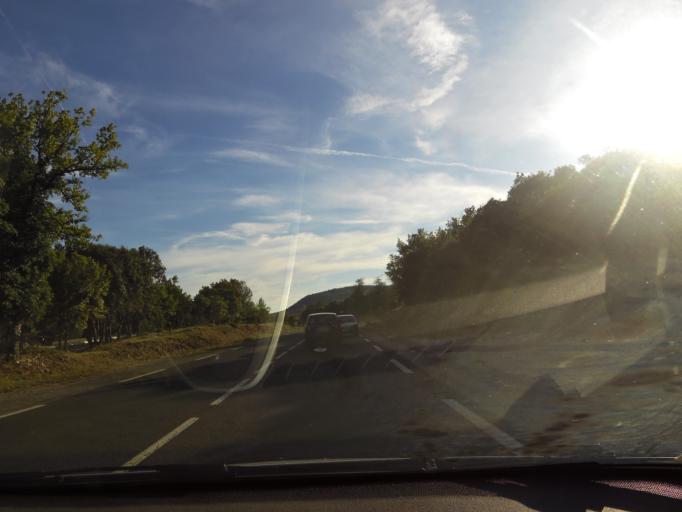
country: FR
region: Languedoc-Roussillon
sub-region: Departement de l'Herault
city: Claret
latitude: 43.8568
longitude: 3.9317
